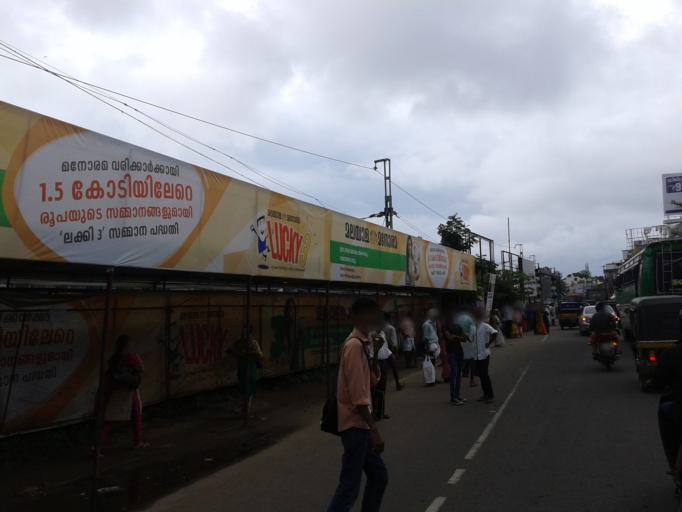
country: IN
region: Kerala
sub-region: Kozhikode
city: Kozhikode
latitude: 11.2508
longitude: 75.7799
